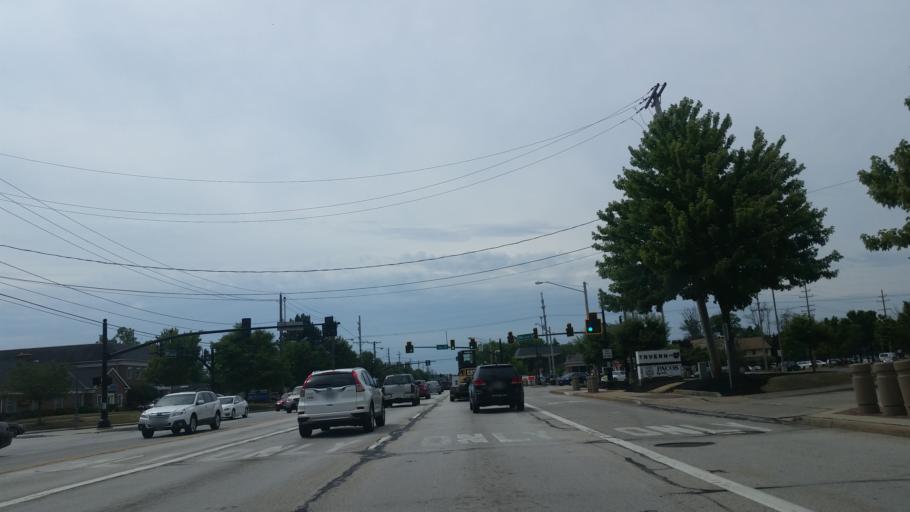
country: US
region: Ohio
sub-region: Cuyahoga County
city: Solon
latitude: 41.3927
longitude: -81.4378
